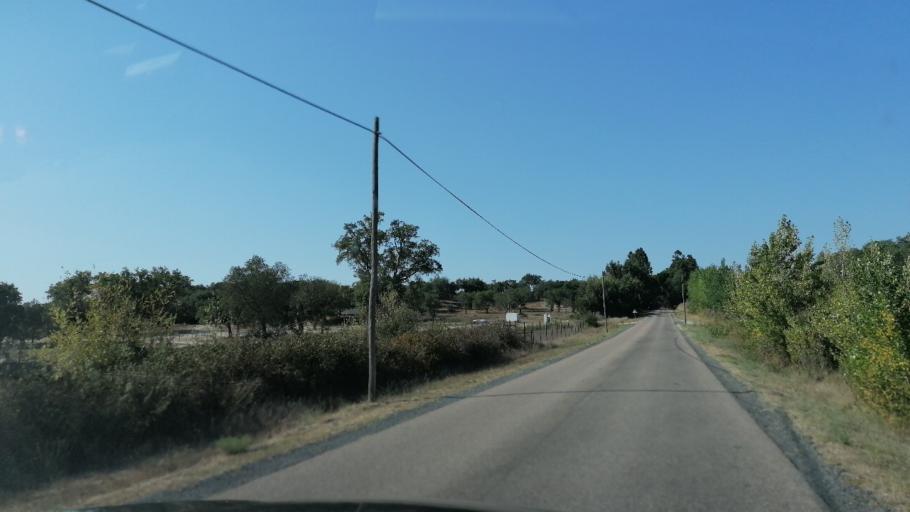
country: PT
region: Santarem
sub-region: Coruche
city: Coruche
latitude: 38.7998
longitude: -8.5788
